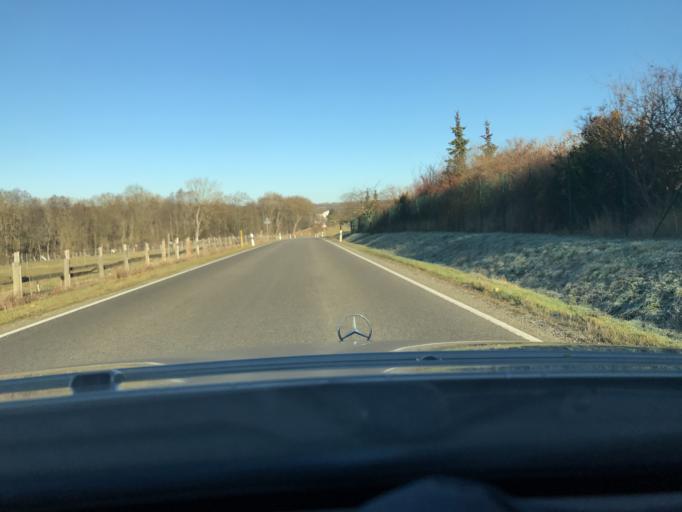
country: DE
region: Thuringia
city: Muehlhausen
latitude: 51.2426
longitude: 10.4671
